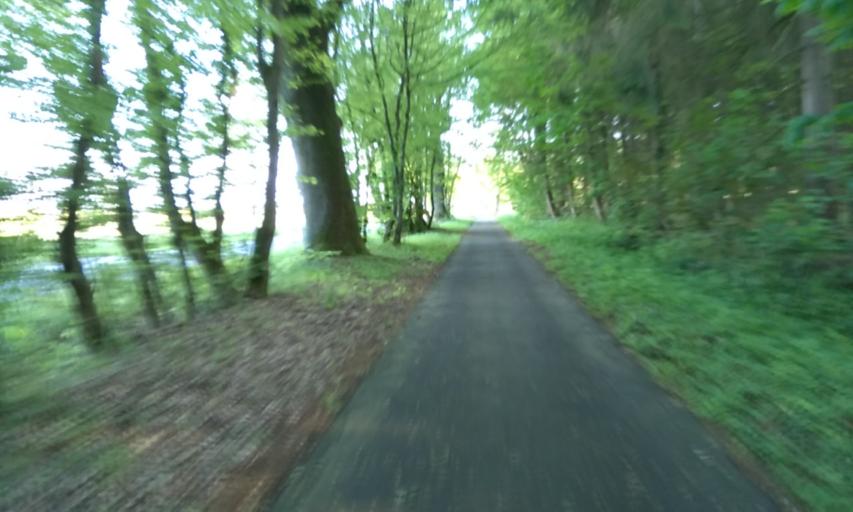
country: DE
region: Lower Saxony
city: Wohnste
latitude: 53.3944
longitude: 9.5392
